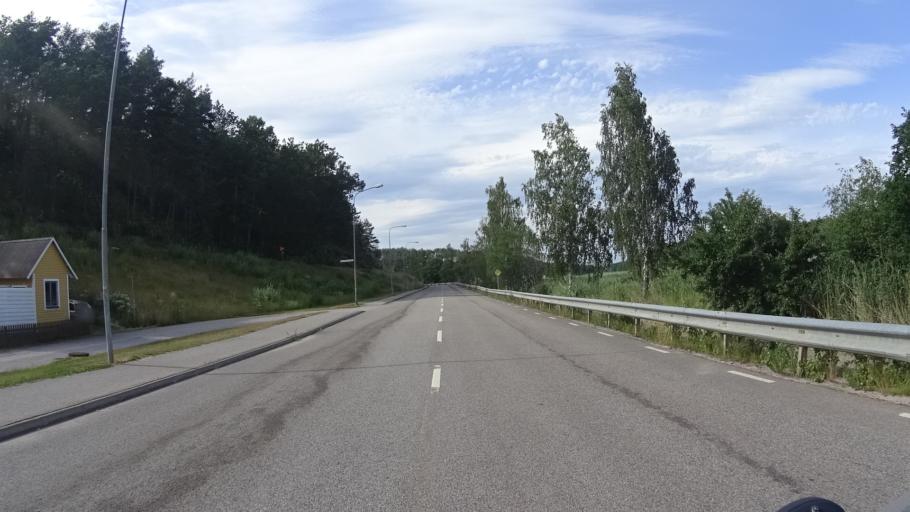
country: SE
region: Kalmar
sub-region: Vasterviks Kommun
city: Gamleby
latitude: 57.8928
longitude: 16.4160
